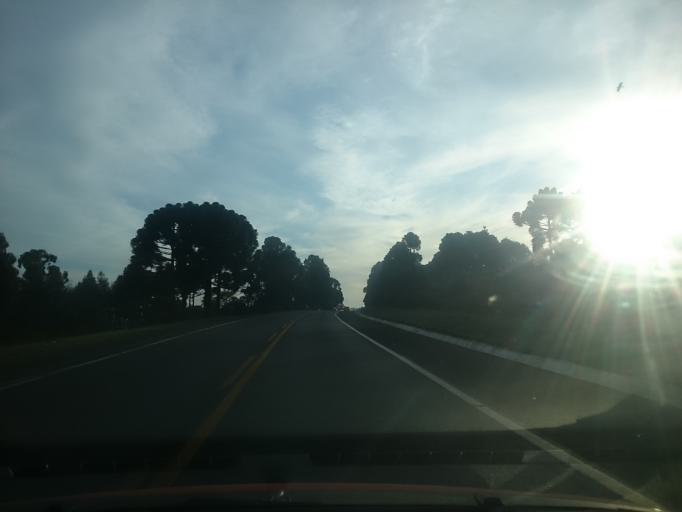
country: BR
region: Rio Grande do Sul
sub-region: Vacaria
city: Estrela
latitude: -28.2723
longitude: -50.7942
